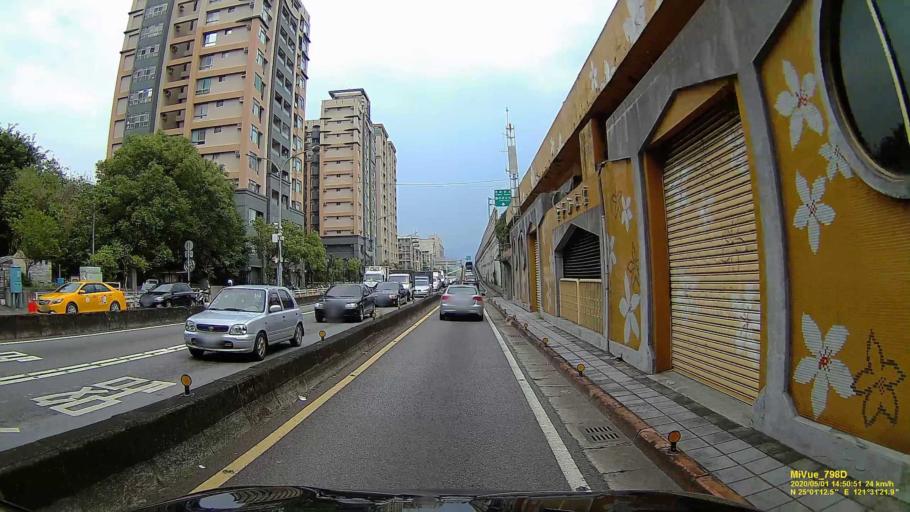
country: TW
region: Taipei
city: Taipei
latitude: 25.0199
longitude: 121.5229
